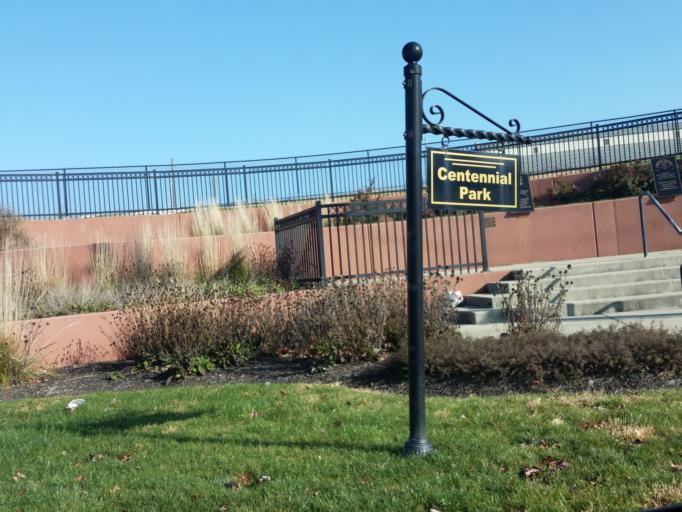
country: US
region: Indiana
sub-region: Marion County
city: Beech Grove
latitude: 39.7196
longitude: -86.0823
